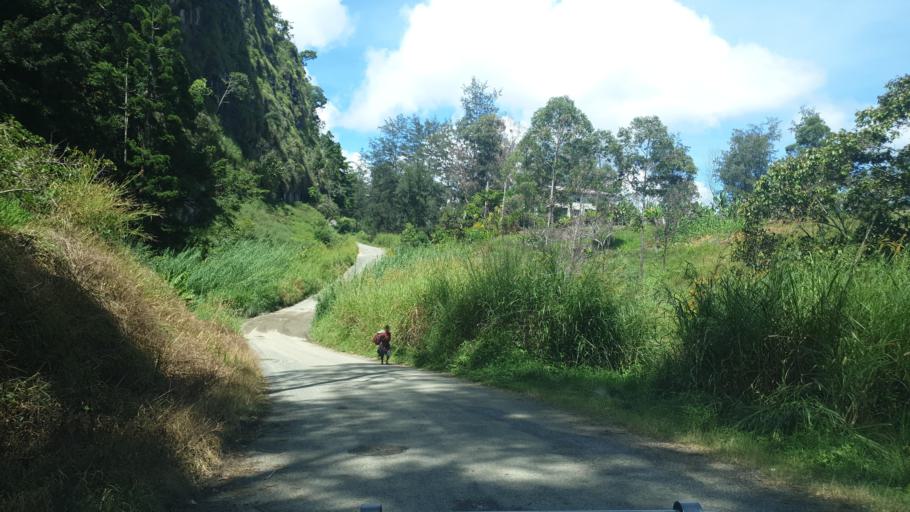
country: PG
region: Chimbu
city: Kundiawa
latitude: -6.1477
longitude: 145.1342
